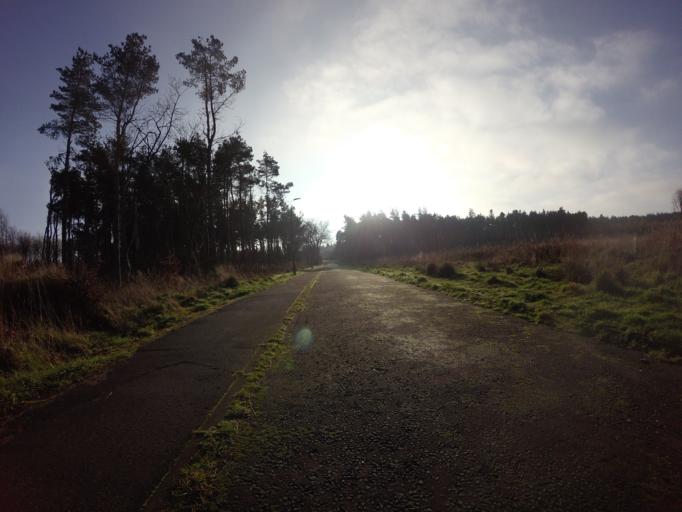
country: GB
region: Scotland
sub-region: West Lothian
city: Livingston
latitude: 55.9196
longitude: -3.5340
